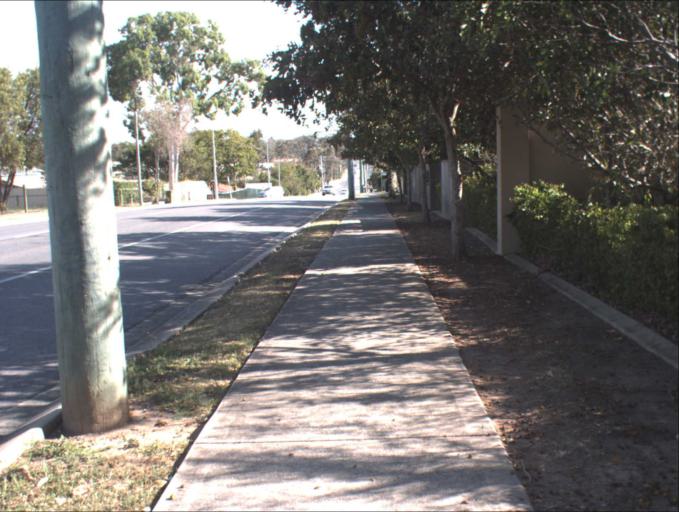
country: AU
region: Queensland
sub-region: Logan
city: Beenleigh
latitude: -27.6966
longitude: 153.2141
